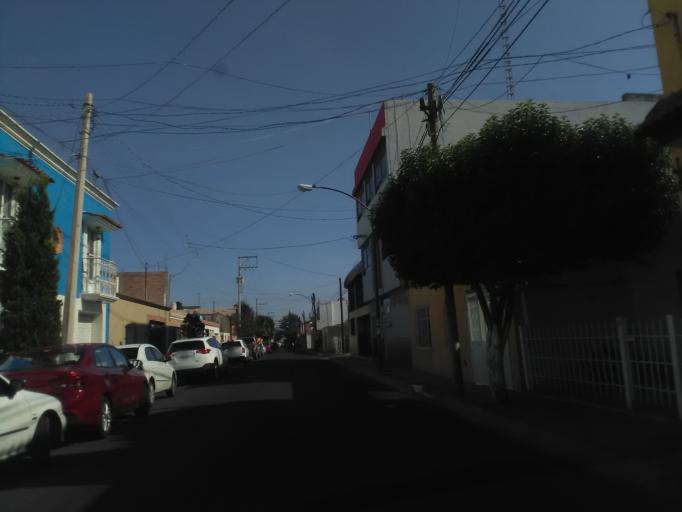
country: MX
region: Durango
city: Victoria de Durango
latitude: 24.0344
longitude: -104.6624
